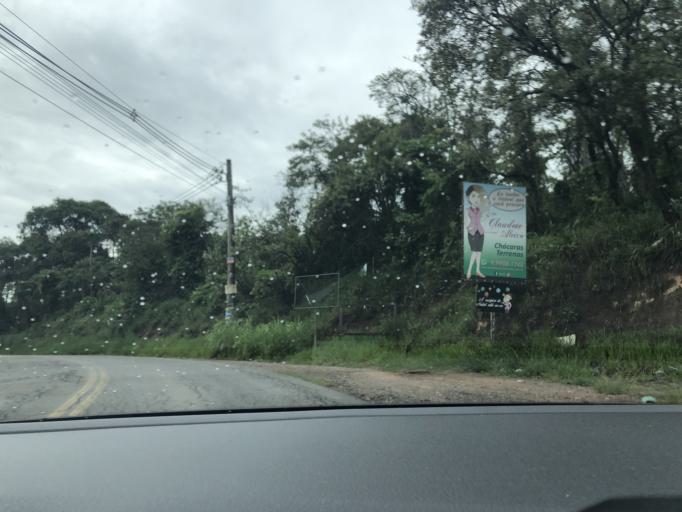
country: BR
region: Sao Paulo
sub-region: Jarinu
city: Jarinu
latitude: -23.1229
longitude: -46.7220
